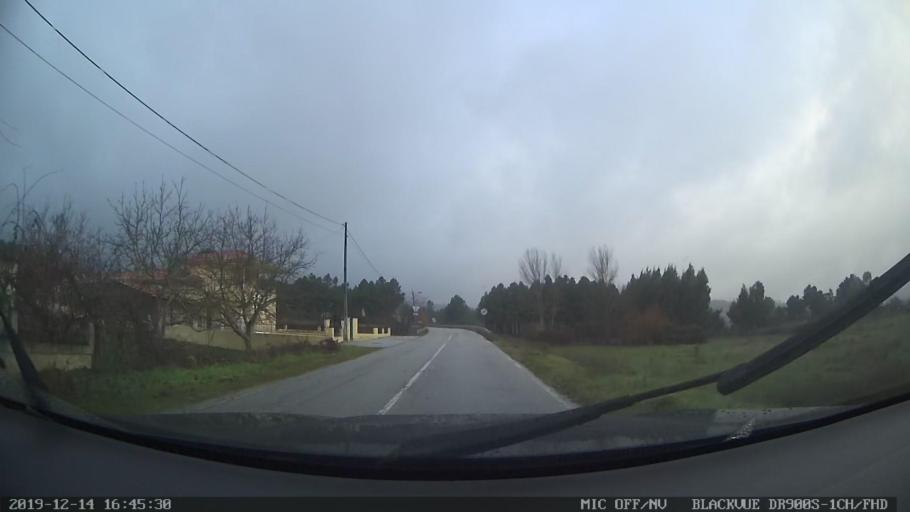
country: PT
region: Vila Real
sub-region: Murca
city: Murca
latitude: 41.3993
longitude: -7.4881
